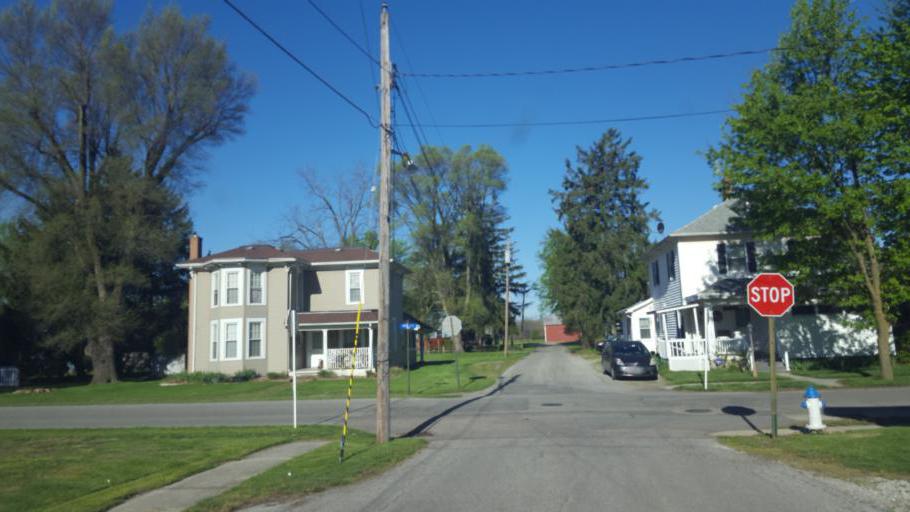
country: US
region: Ohio
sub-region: Morrow County
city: Cardington
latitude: 40.6355
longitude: -82.9699
